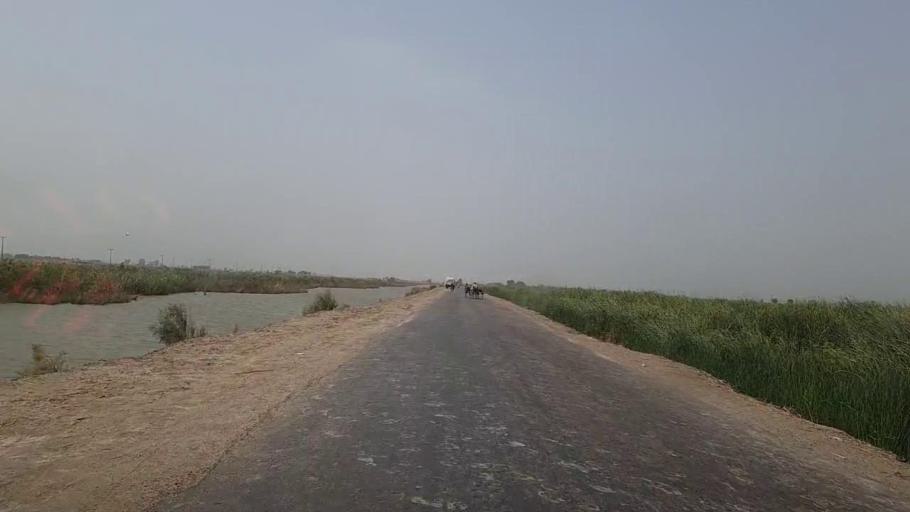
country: PK
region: Sindh
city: Radhan
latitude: 27.1550
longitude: 67.9403
